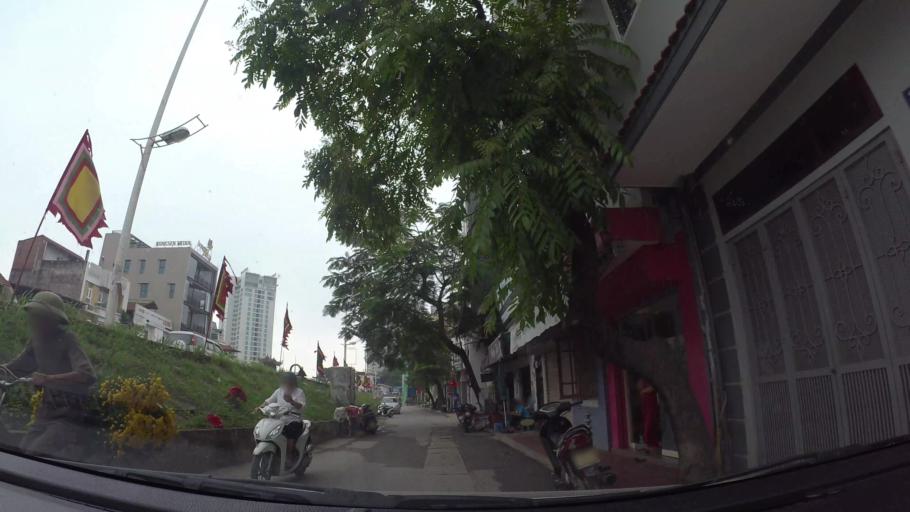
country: VN
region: Ha Noi
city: Tay Ho
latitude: 21.0659
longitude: 105.8311
